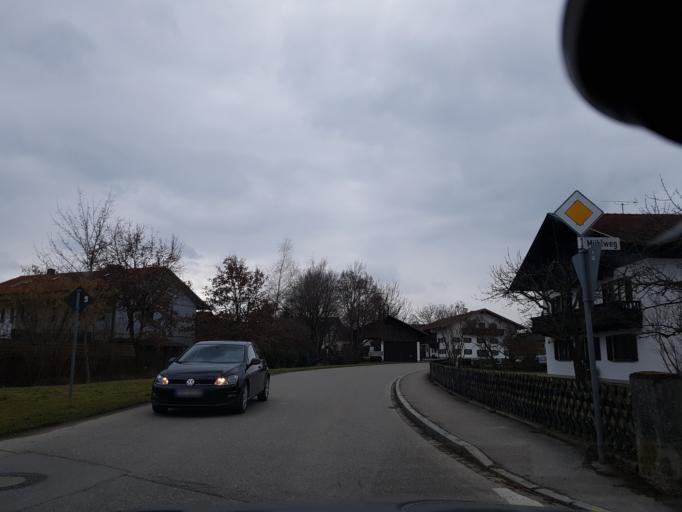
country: DE
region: Bavaria
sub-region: Upper Bavaria
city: Bad Aibling
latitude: 47.8556
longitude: 11.9891
